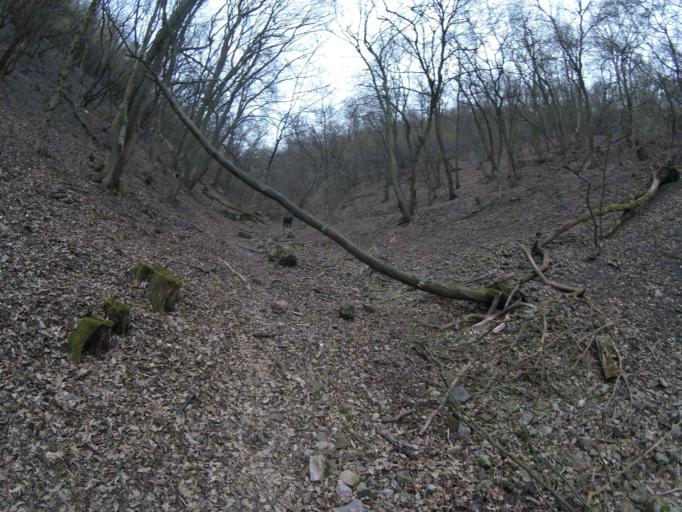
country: HU
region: Pest
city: Szob
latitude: 47.8132
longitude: 18.8186
